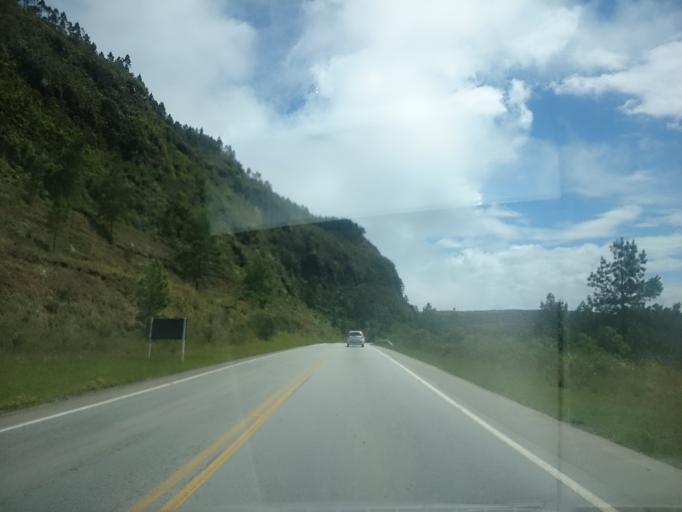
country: BR
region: Santa Catarina
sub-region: Anitapolis
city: Anitapolis
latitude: -27.6902
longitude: -49.1233
